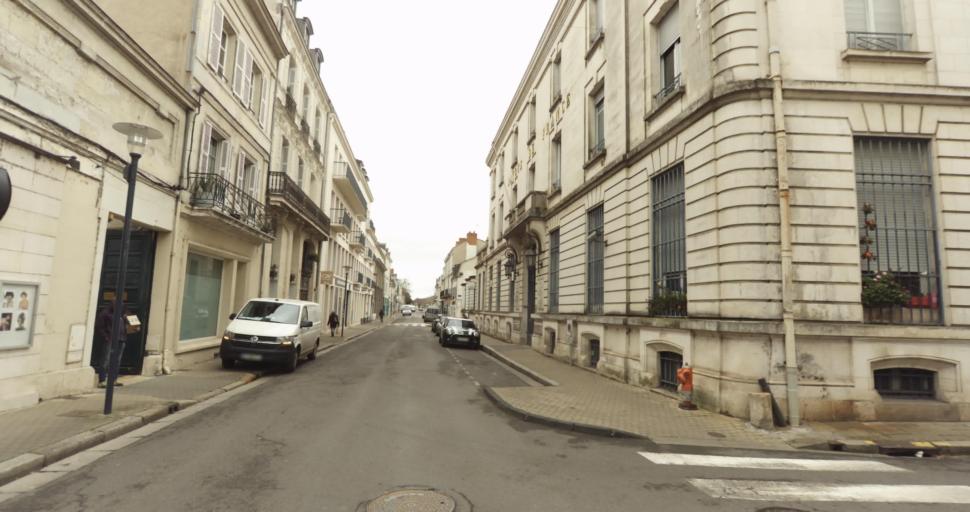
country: FR
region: Pays de la Loire
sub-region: Departement de Maine-et-Loire
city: Saumur
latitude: 47.2598
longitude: -0.0798
